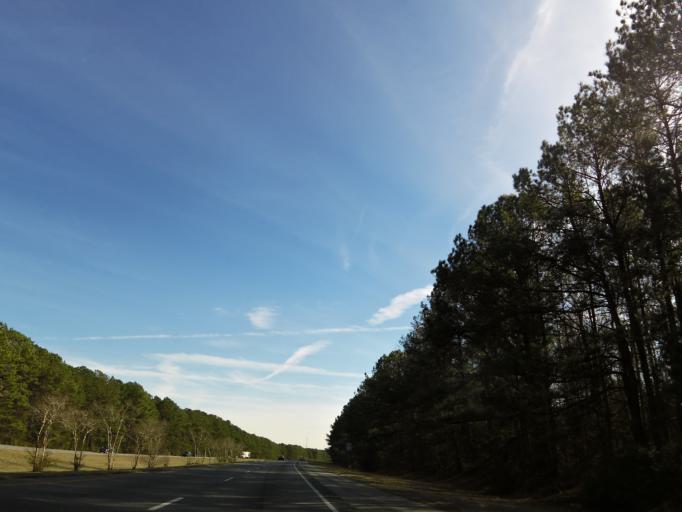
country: US
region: Georgia
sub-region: Harris County
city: Hamilton
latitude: 32.6554
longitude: -84.9753
